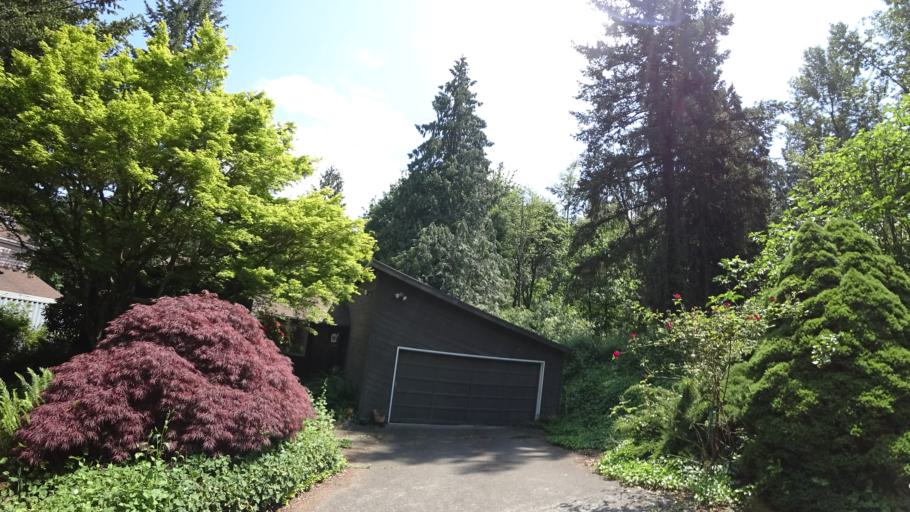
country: US
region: Oregon
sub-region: Clackamas County
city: Happy Valley
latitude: 45.4721
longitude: -122.5156
